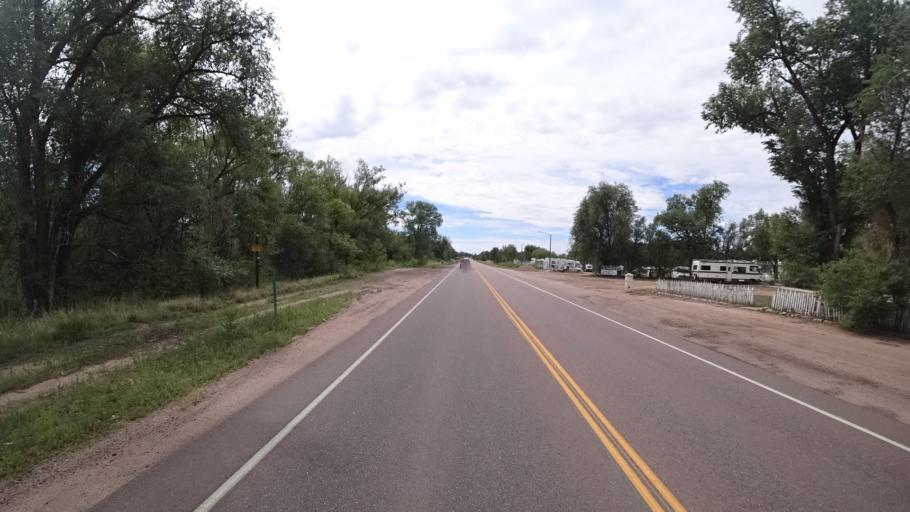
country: US
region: Colorado
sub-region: El Paso County
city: Fountain
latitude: 38.7052
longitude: -104.7101
